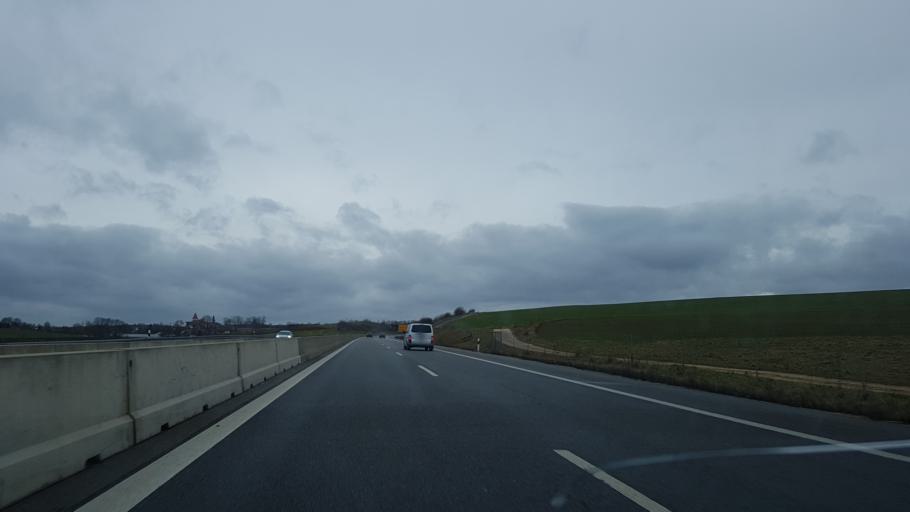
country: DE
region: Bavaria
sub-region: Upper Palatinate
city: Schierling
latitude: 48.8440
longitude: 12.1098
